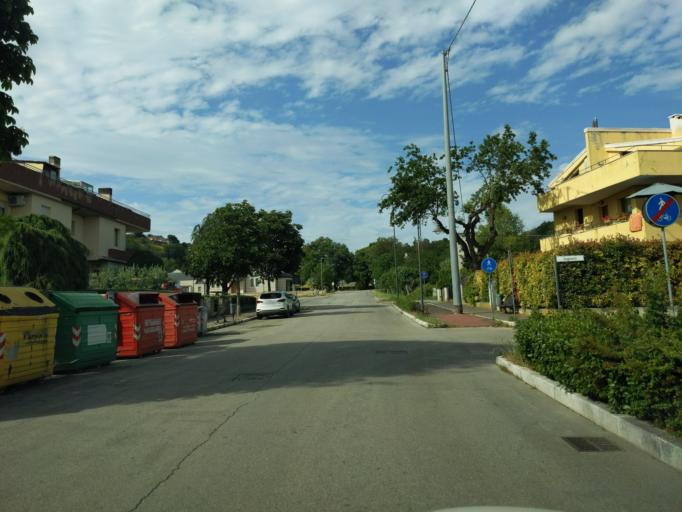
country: IT
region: The Marches
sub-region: Provincia di Pesaro e Urbino
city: Gradara
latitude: 43.9553
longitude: 12.7734
